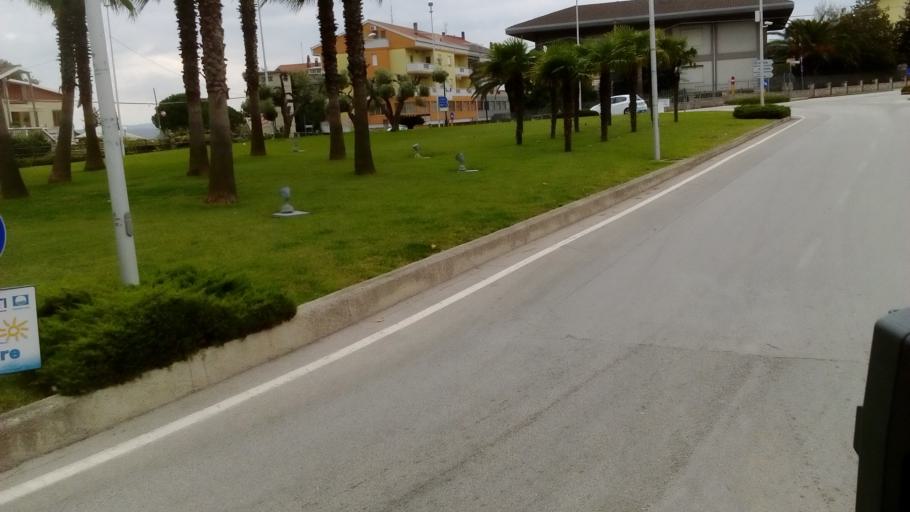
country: IT
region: Abruzzo
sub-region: Provincia di Chieti
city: San Salvo
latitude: 42.0551
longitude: 14.7337
